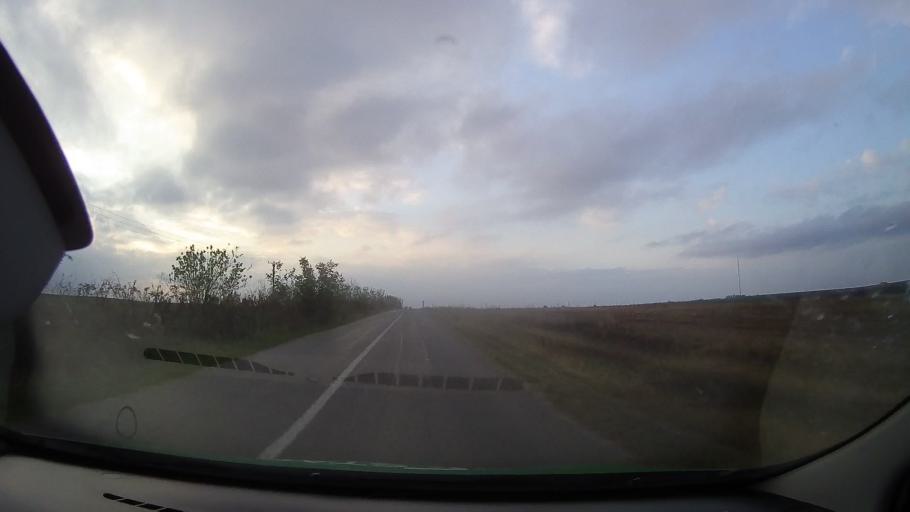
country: RO
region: Constanta
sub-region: Comuna Dobromir
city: Dobromir
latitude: 44.0343
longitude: 27.7642
